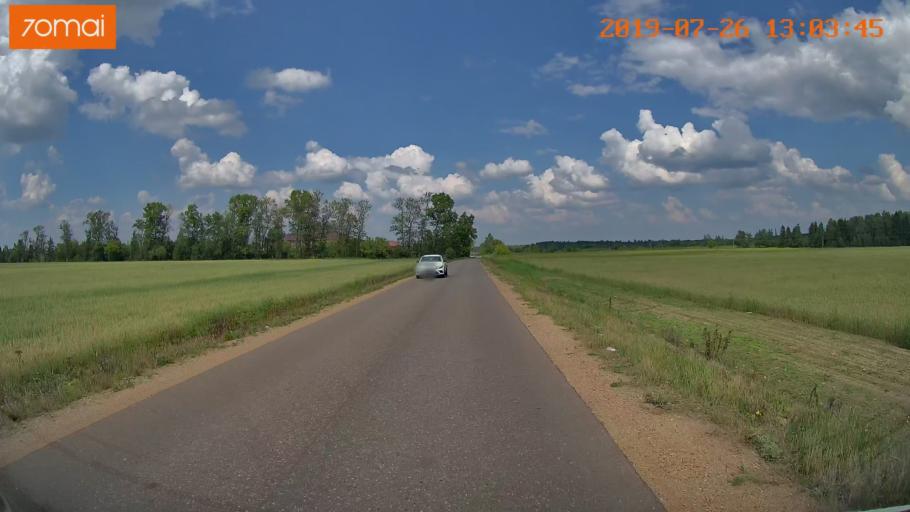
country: RU
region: Ivanovo
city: Bogorodskoye
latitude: 57.0491
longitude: 41.0220
